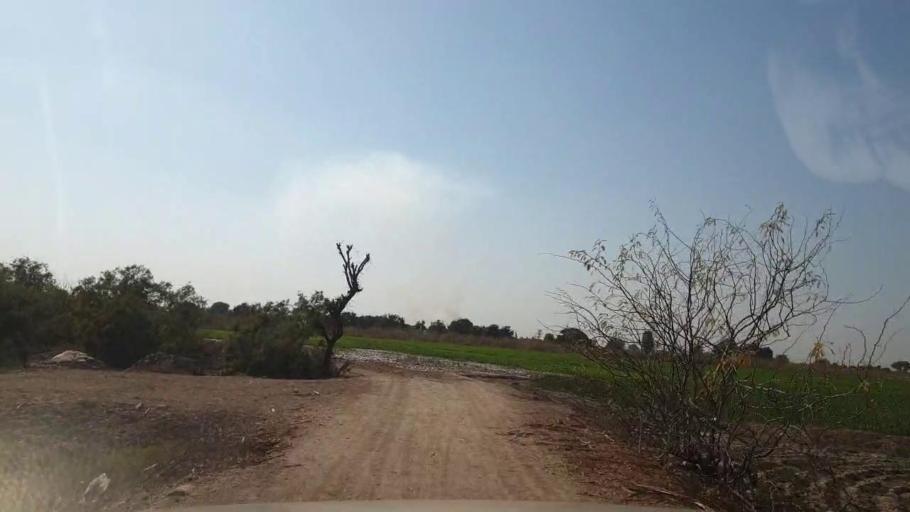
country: PK
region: Sindh
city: Tando Allahyar
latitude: 25.4805
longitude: 68.6750
